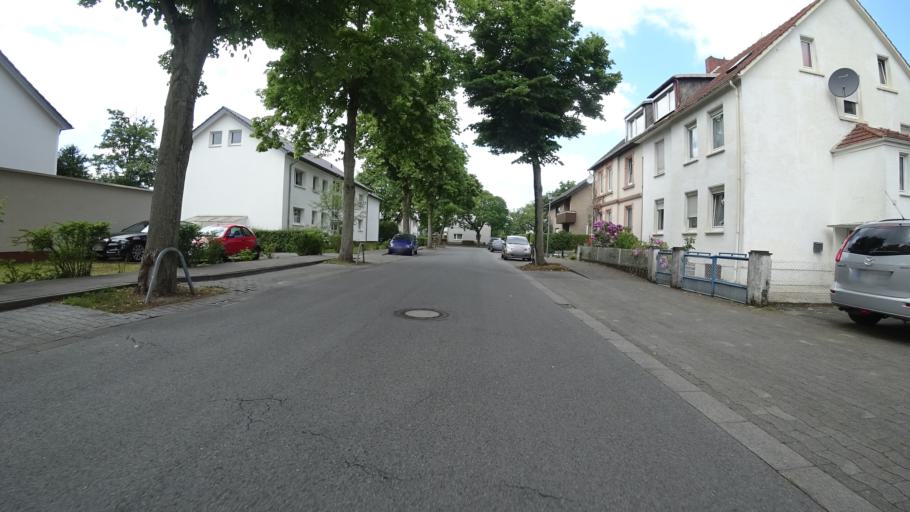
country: DE
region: North Rhine-Westphalia
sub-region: Regierungsbezirk Detmold
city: Guetersloh
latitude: 51.9159
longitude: 8.3751
